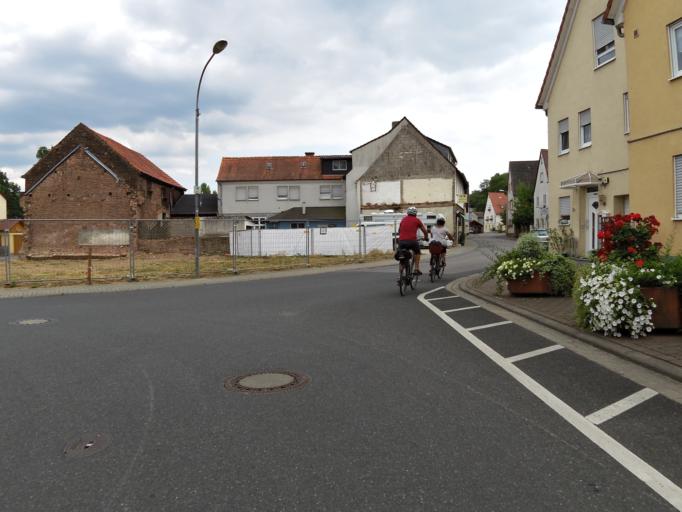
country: DE
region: Bavaria
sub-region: Regierungsbezirk Unterfranken
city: Obernburg am Main
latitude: 49.8334
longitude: 9.1125
